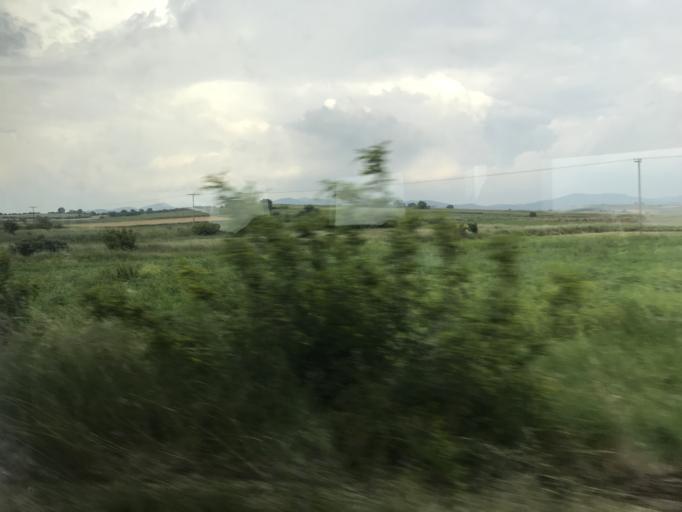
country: GR
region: East Macedonia and Thrace
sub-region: Nomos Rodopis
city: Sapes
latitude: 40.9947
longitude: 25.6602
